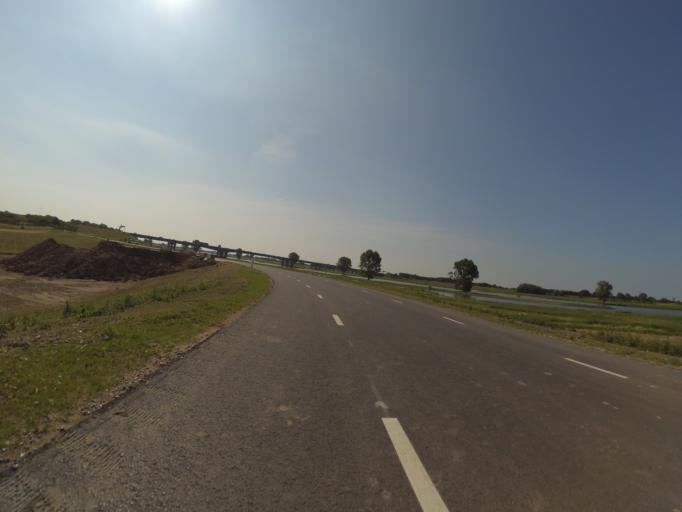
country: NL
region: Utrecht
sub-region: Gemeente Vianen
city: Vianen
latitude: 52.0057
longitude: 5.1090
